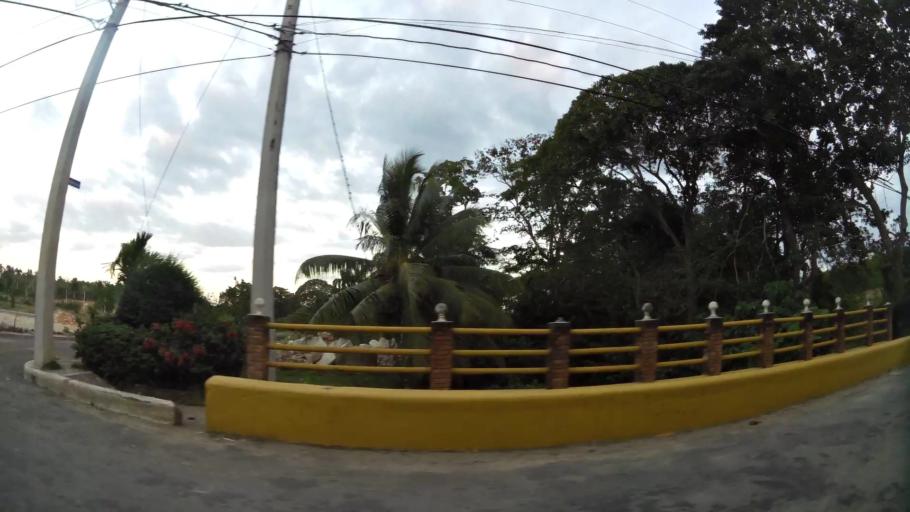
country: DO
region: Nacional
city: La Agustina
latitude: 18.5641
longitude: -69.9374
